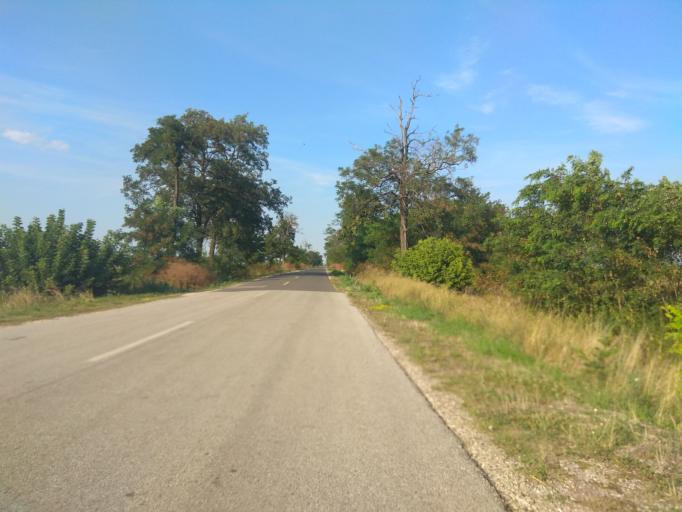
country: HU
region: Borsod-Abauj-Zemplen
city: Emod
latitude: 47.8795
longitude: 20.7634
